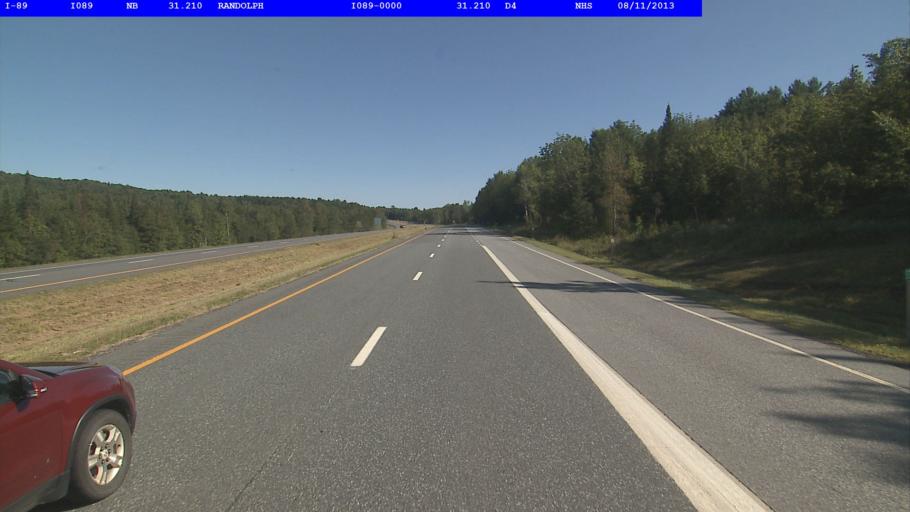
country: US
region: Vermont
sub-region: Orange County
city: Randolph
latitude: 43.9490
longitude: -72.6216
